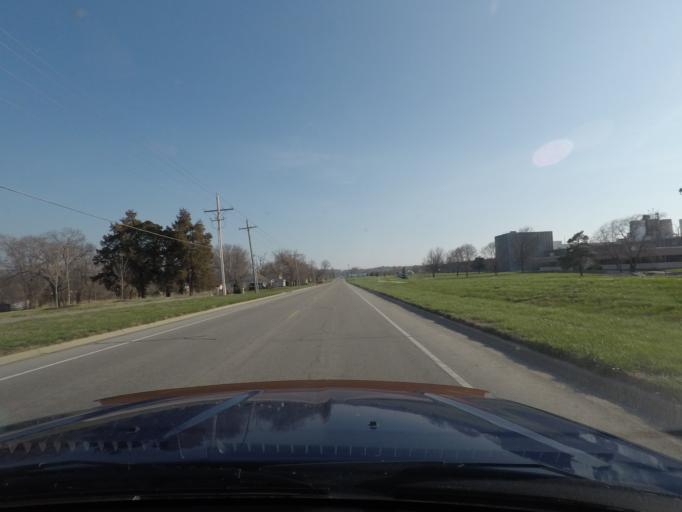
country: US
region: Kansas
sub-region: Douglas County
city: Lawrence
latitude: 38.9974
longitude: -95.2605
